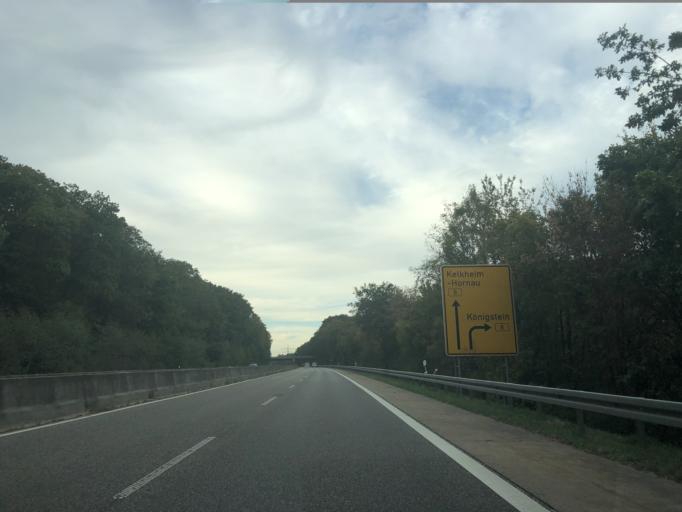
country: DE
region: Hesse
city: Kelkheim (Taunus)
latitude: 50.1471
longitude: 8.4714
